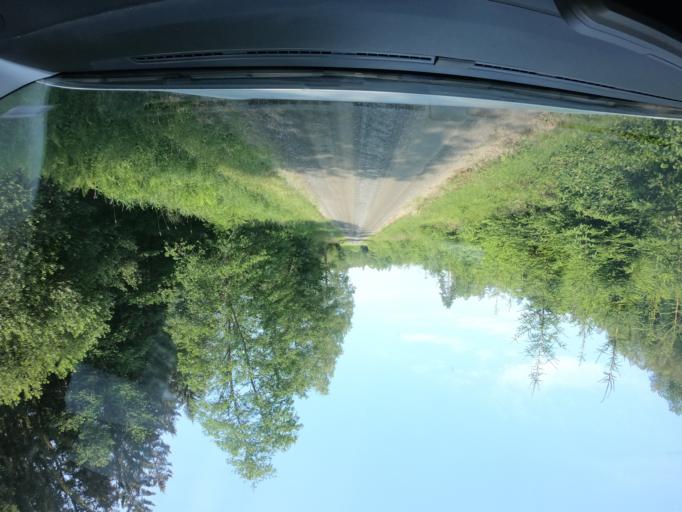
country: SE
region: Skane
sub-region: Hassleholms Kommun
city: Bjarnum
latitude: 56.2356
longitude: 13.6495
